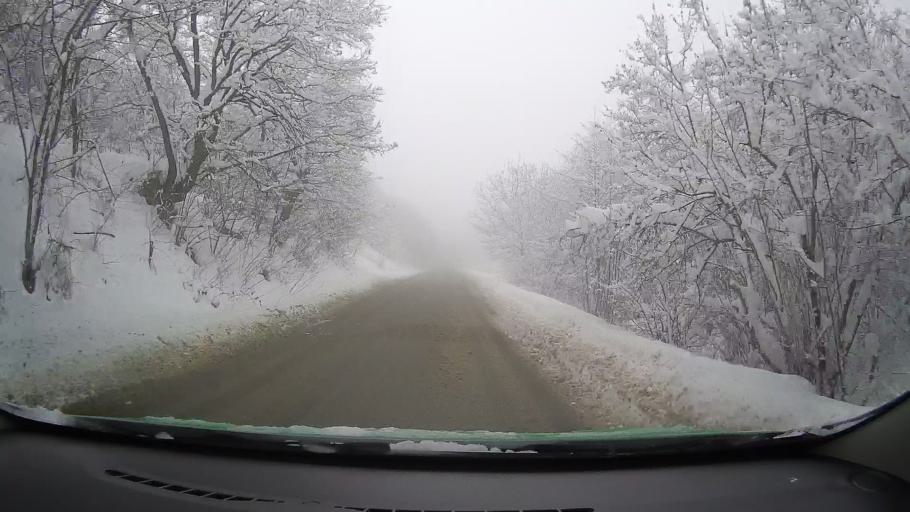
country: RO
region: Sibiu
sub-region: Comuna Poiana Sibiului
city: Poiana Sibiului
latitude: 45.8084
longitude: 23.7666
